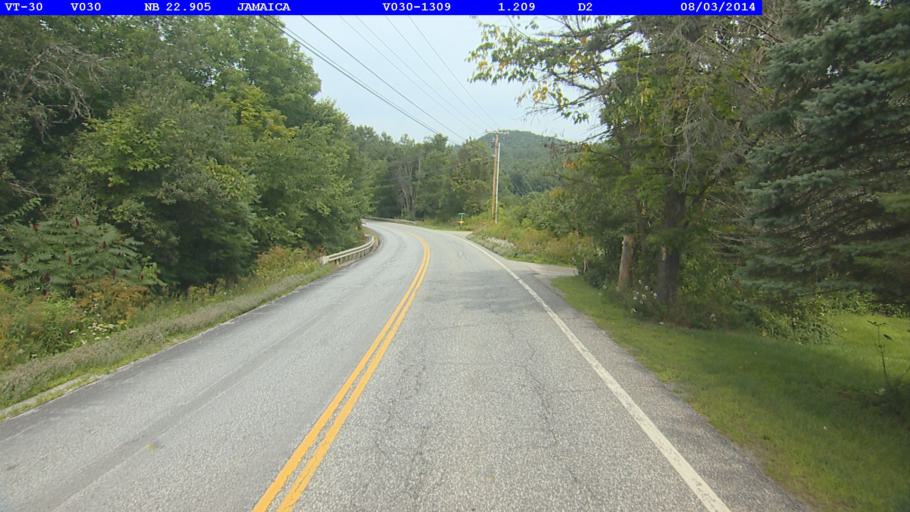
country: US
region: Vermont
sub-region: Windham County
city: Newfane
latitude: 43.0800
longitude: -72.7426
